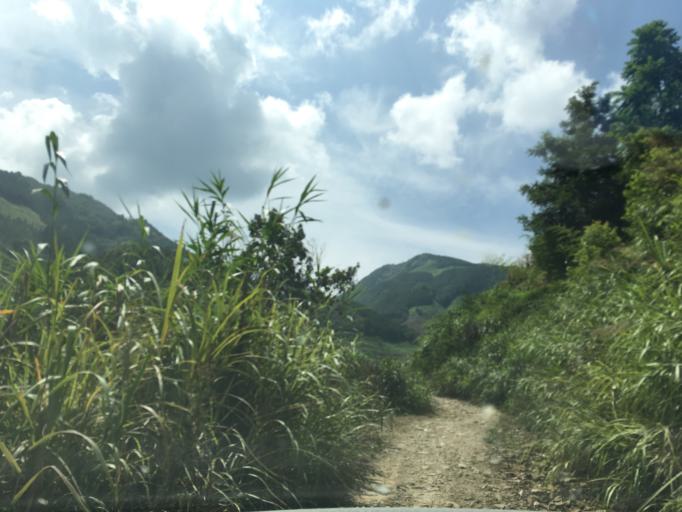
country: CN
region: Guangxi Zhuangzu Zizhiqu
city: Xinzhou
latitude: 24.9533
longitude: 105.7875
